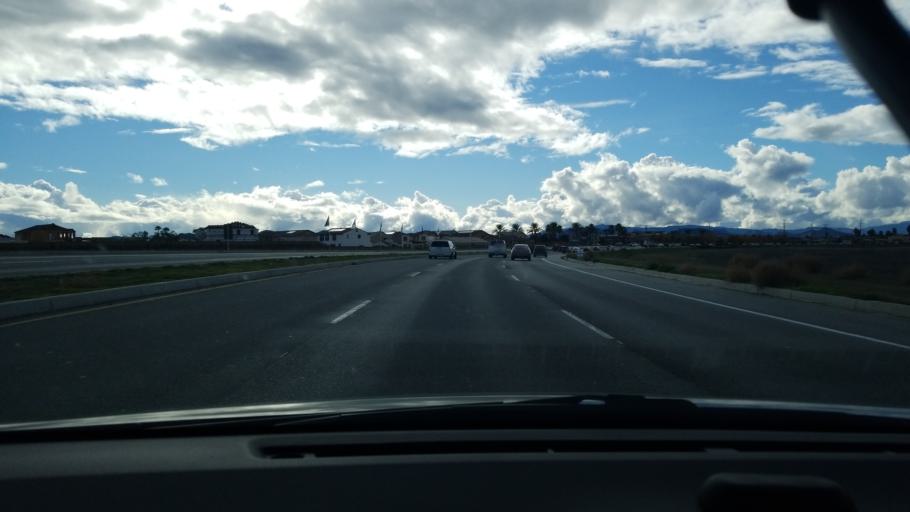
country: US
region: California
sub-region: Riverside County
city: Menifee
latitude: 33.6864
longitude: -117.1459
